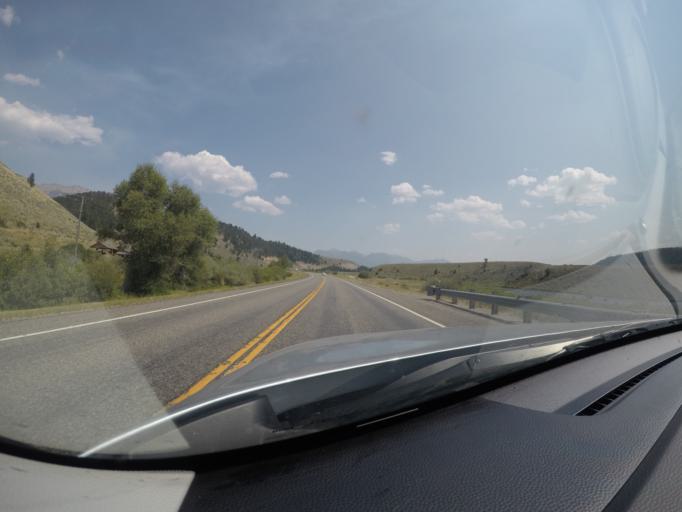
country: US
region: Montana
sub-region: Gallatin County
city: Big Sky
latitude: 44.8671
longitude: -111.5585
